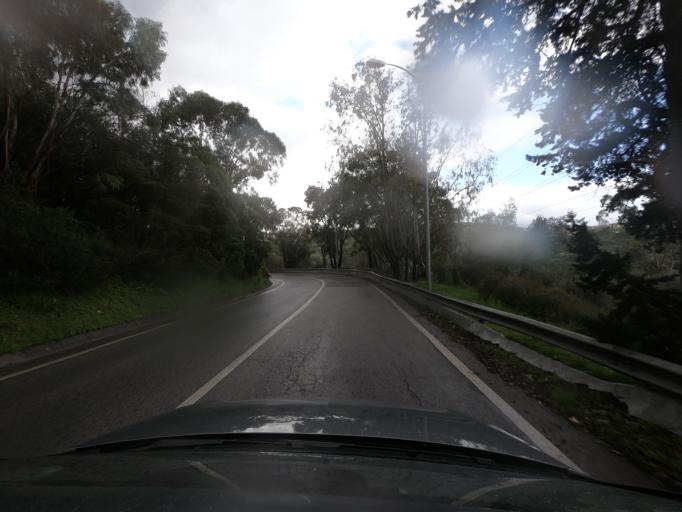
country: PT
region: Lisbon
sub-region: Oeiras
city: Carnaxide
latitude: 38.7268
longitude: -9.2565
